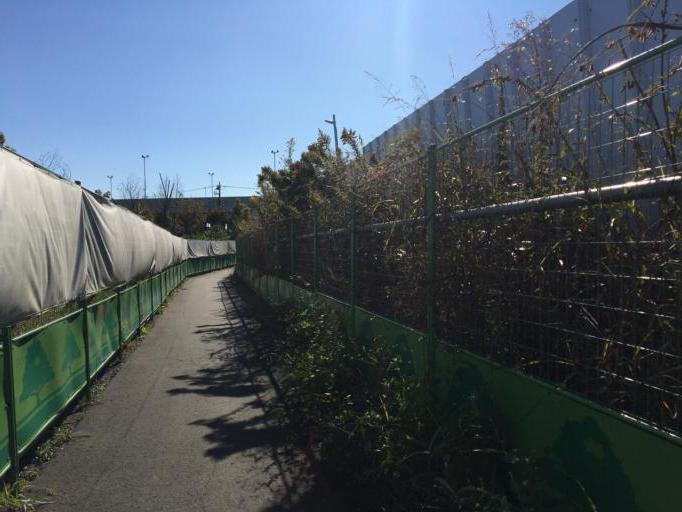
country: JP
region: Saitama
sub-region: Kawaguchi-shi
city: Hatogaya-honcho
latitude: 35.8479
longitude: 139.7417
